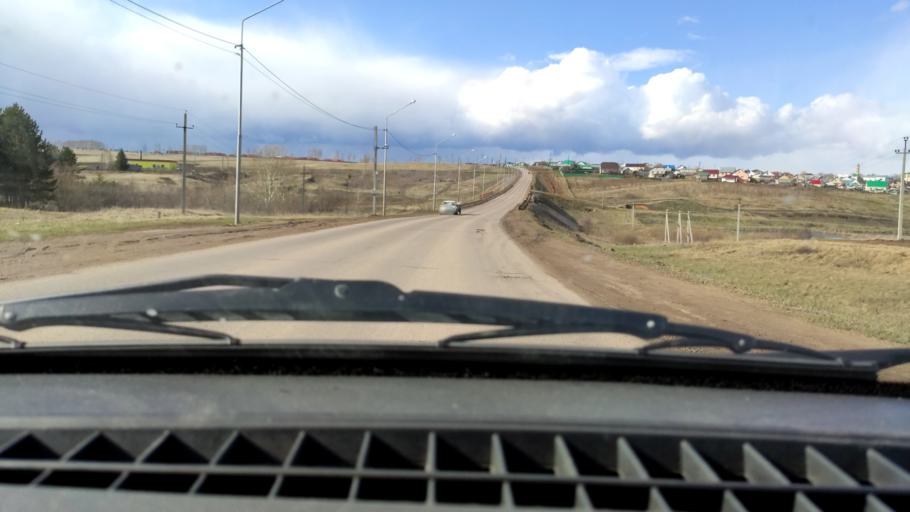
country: RU
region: Bashkortostan
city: Chekmagush
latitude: 55.1311
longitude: 54.6357
